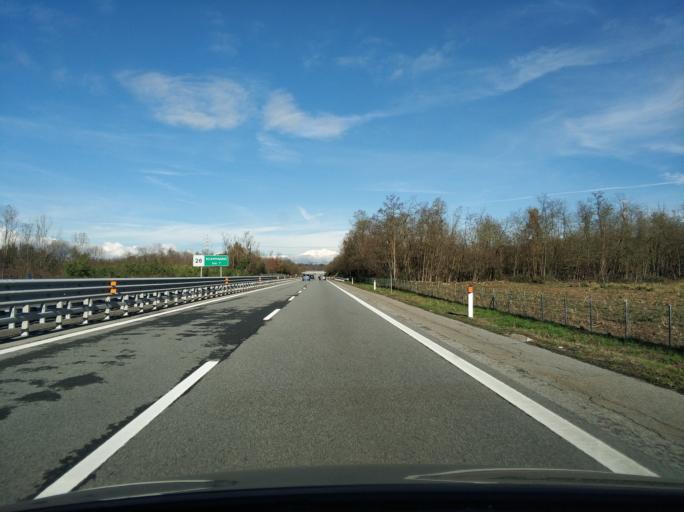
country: IT
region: Piedmont
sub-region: Provincia di Torino
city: Montalenghe
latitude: 45.3277
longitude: 7.8237
